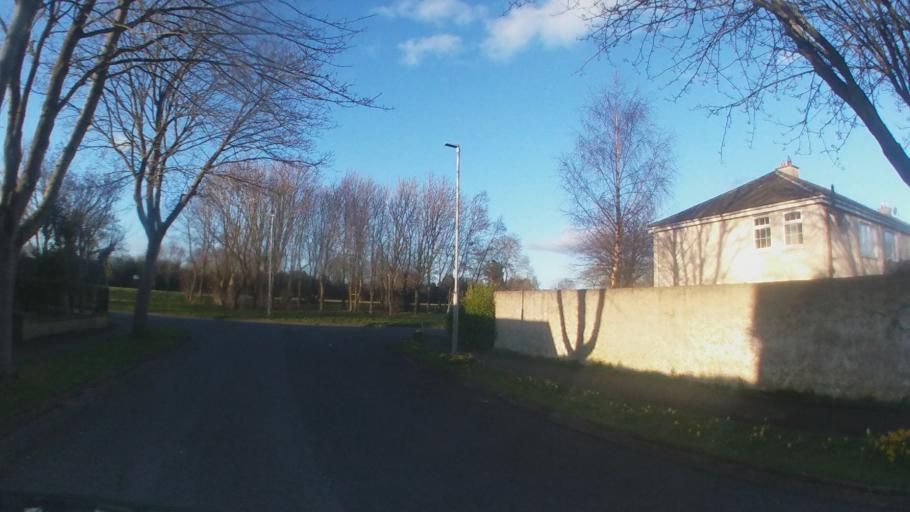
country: IE
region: Leinster
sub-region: Fingal County
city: Blanchardstown
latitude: 53.3766
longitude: -6.3866
